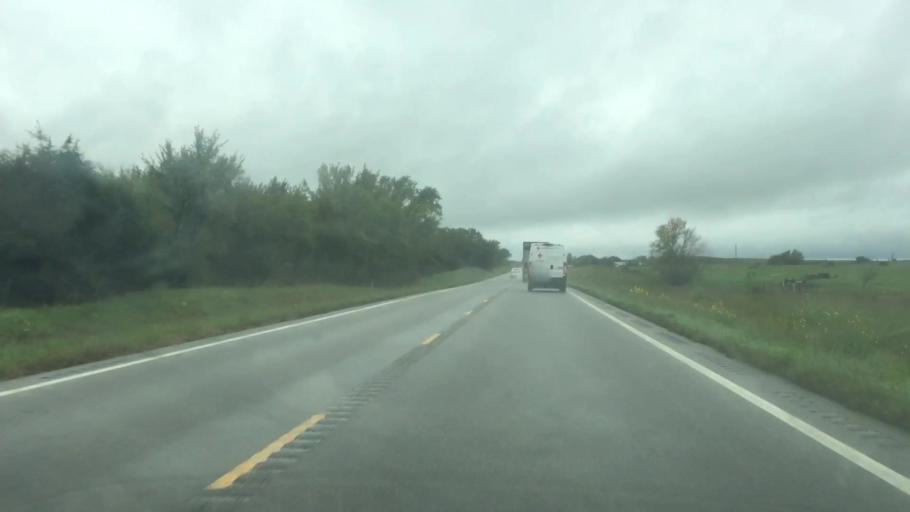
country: US
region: Kansas
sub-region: Allen County
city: Iola
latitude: 38.1015
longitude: -95.3559
